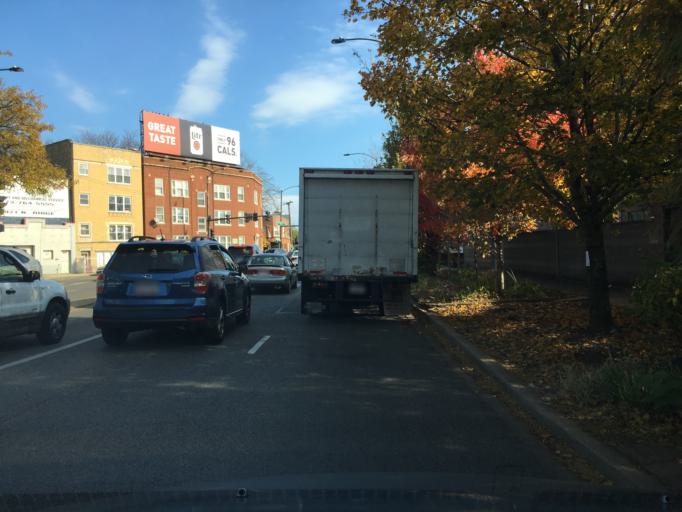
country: US
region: Illinois
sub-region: Cook County
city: Evanston
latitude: 41.9907
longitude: -87.6729
